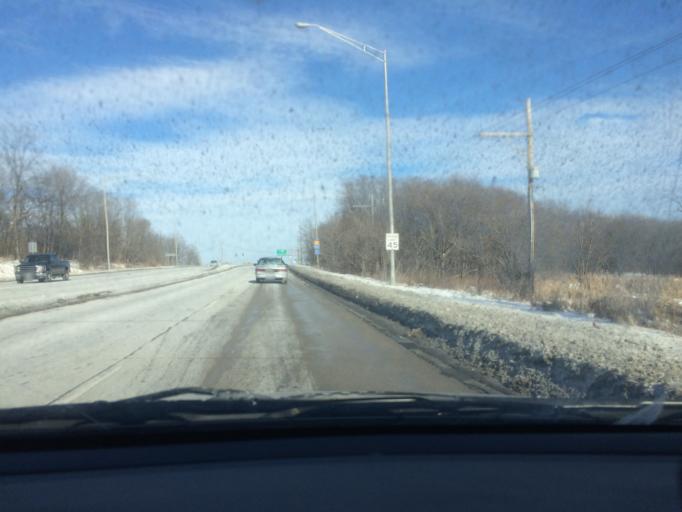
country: US
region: Illinois
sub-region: Cook County
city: Streamwood
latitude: 42.0612
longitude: -88.1934
